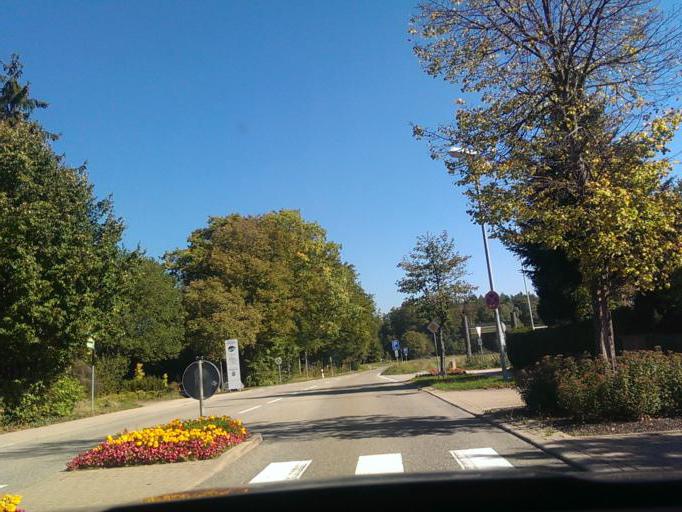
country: DE
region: Baden-Wuerttemberg
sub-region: Karlsruhe Region
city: Dobel
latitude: 48.8013
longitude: 8.5068
